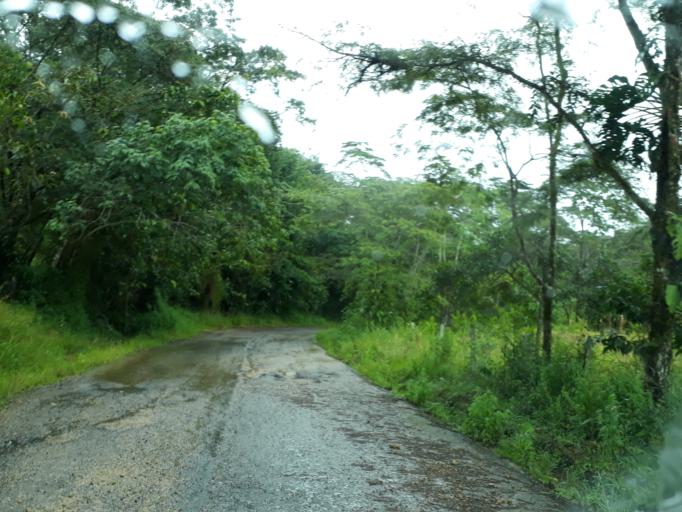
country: CO
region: Cundinamarca
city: Medina
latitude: 4.6565
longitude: -73.3284
